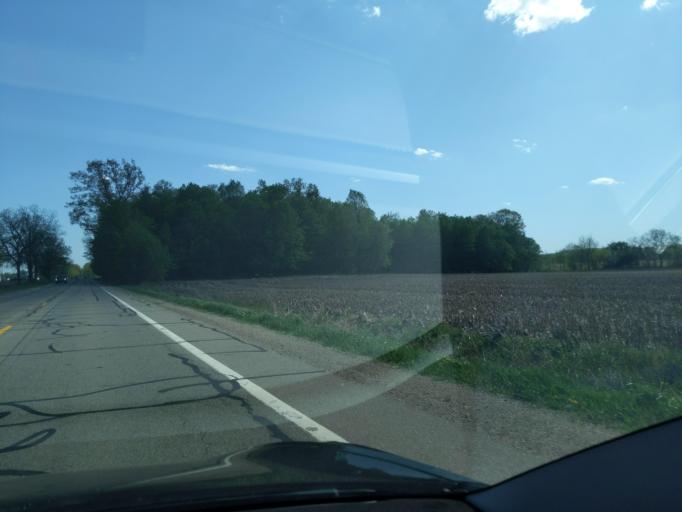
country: US
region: Michigan
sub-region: Kent County
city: Lowell
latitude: 42.8697
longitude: -85.3710
